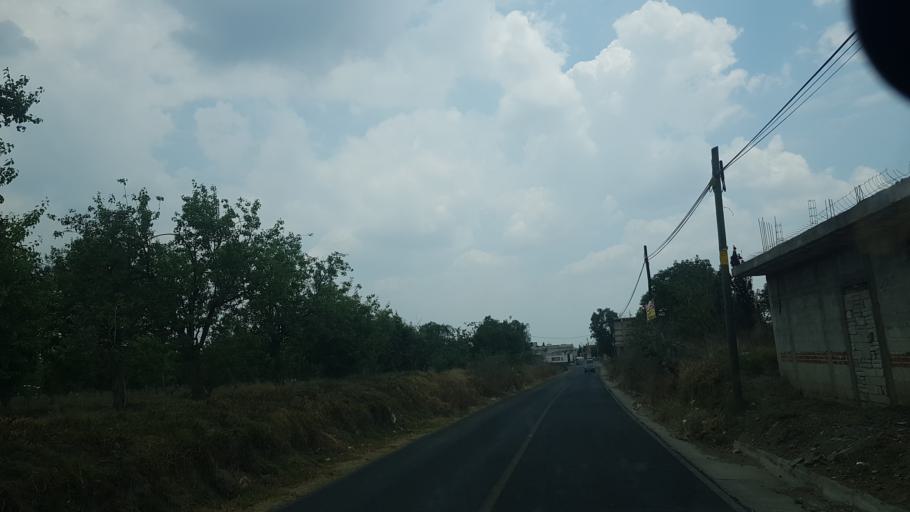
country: MX
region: Puebla
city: Huejotzingo
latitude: 19.1588
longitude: -98.4213
